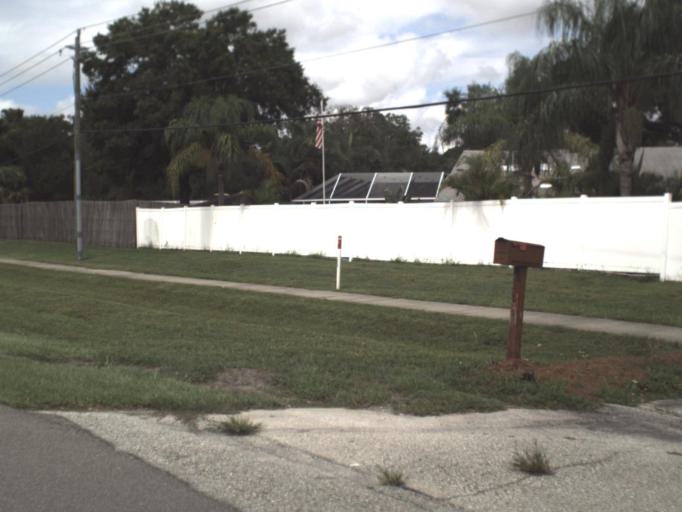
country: US
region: Florida
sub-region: Sarasota County
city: Desoto Lakes
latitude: 27.3886
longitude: -82.4990
